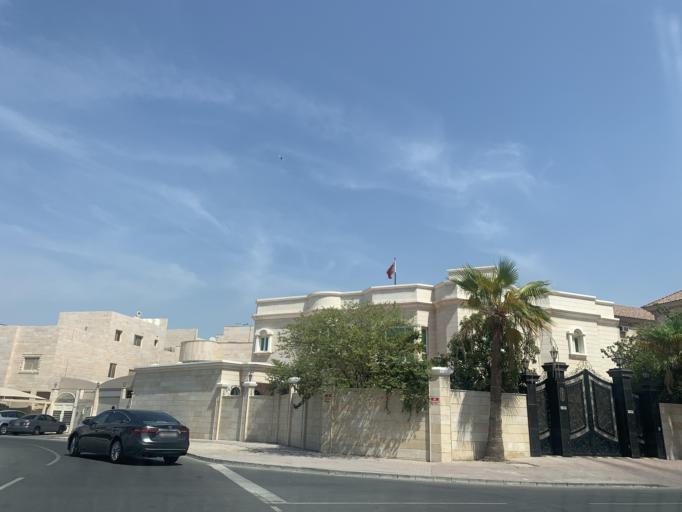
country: BH
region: Central Governorate
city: Madinat Hamad
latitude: 26.1336
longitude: 50.5077
